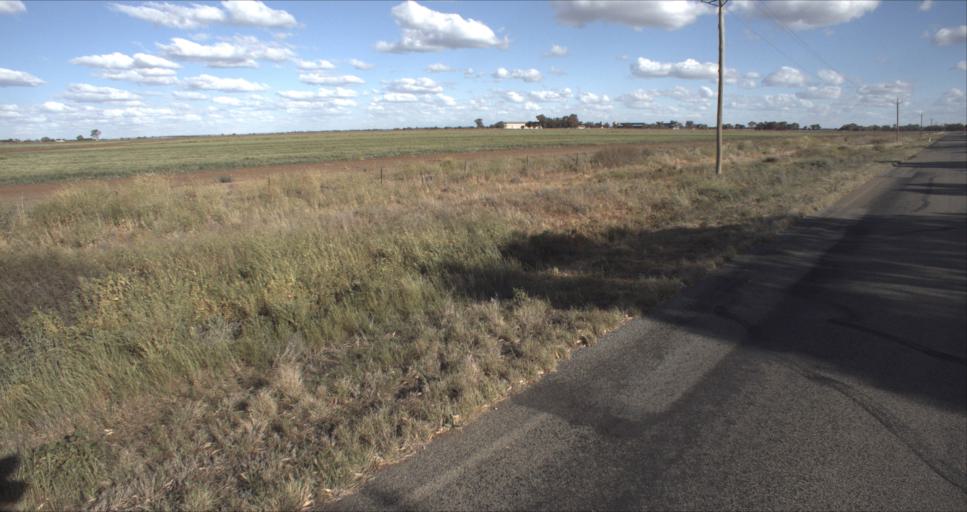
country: AU
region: New South Wales
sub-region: Leeton
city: Leeton
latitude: -34.5456
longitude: 146.2795
